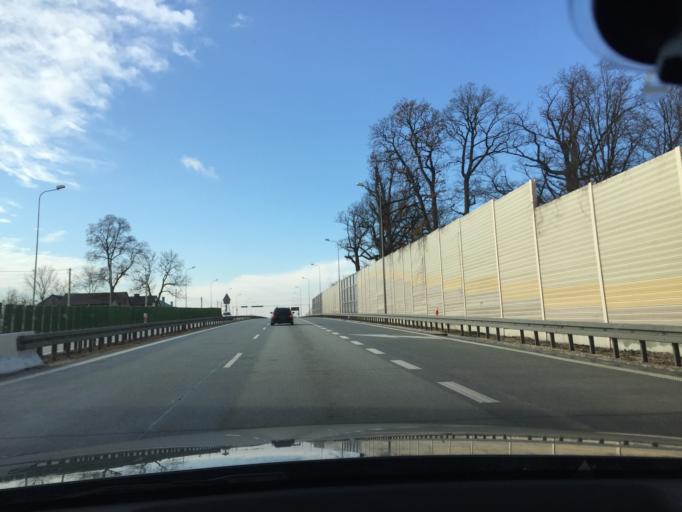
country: PL
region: Lodz Voivodeship
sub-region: Powiat rawski
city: Rawa Mazowiecka
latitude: 51.8039
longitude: 20.3008
